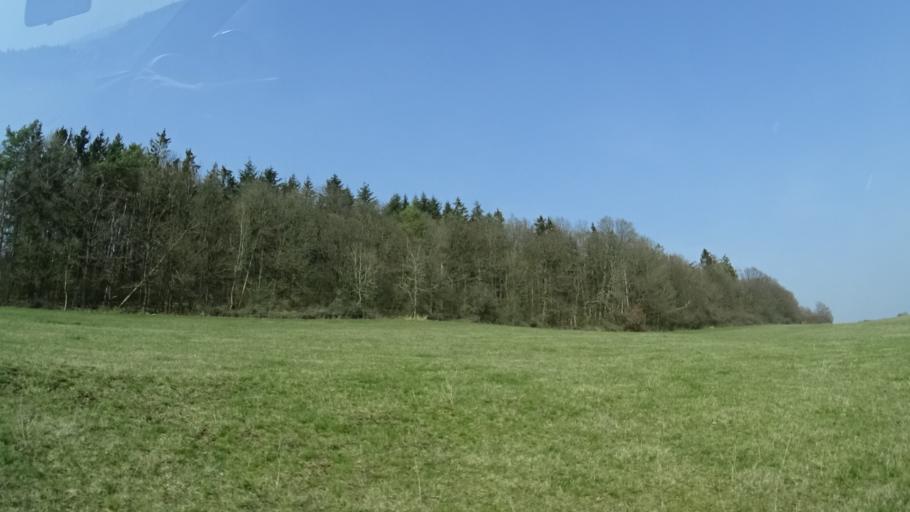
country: DE
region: Rheinland-Pfalz
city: Thallichtenberg
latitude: 49.5763
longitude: 7.3345
